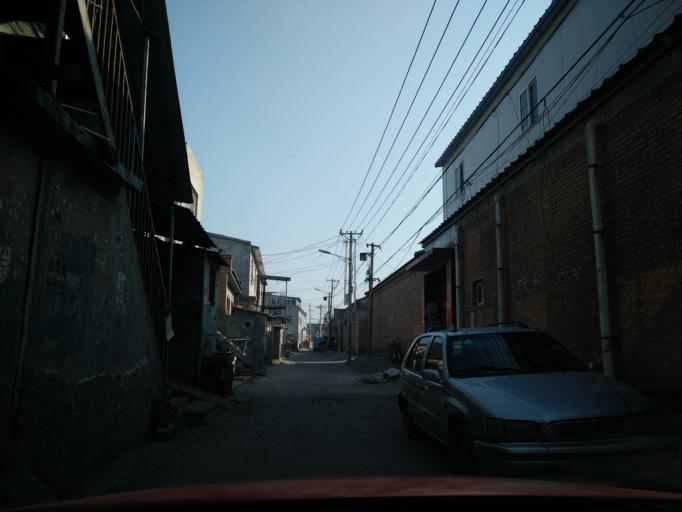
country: CN
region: Beijing
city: Yinghai
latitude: 39.7146
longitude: 116.4521
